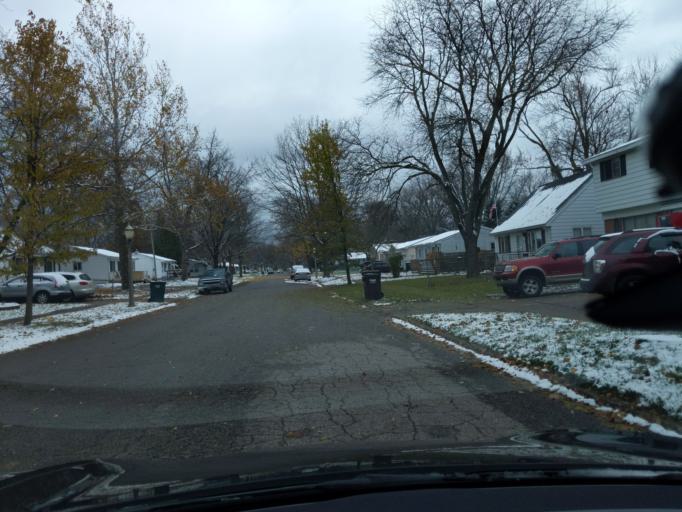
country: US
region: Michigan
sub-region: Ingham County
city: Edgemont Park
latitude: 42.6969
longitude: -84.5916
